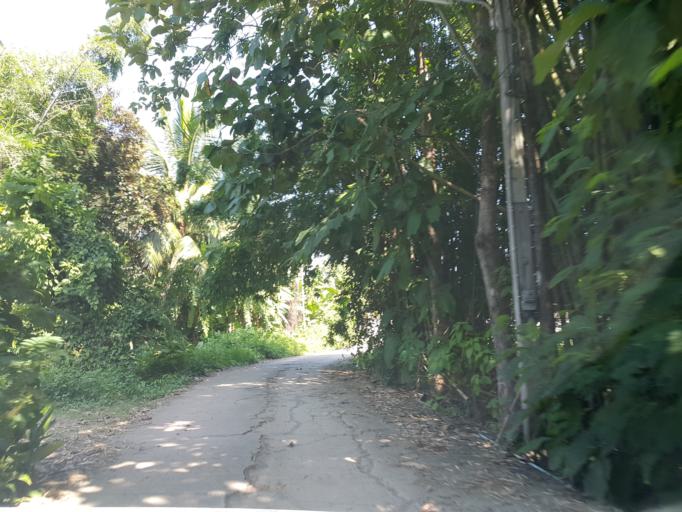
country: TH
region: Chiang Mai
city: San Kamphaeng
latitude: 18.7470
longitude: 99.1696
